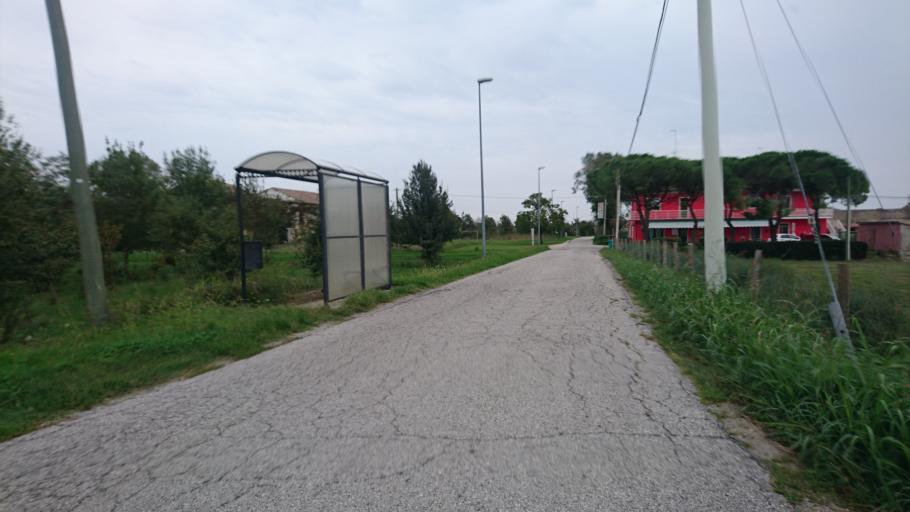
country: IT
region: Emilia-Romagna
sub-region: Provincia di Ferrara
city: Goro
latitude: 44.8669
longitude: 12.3612
